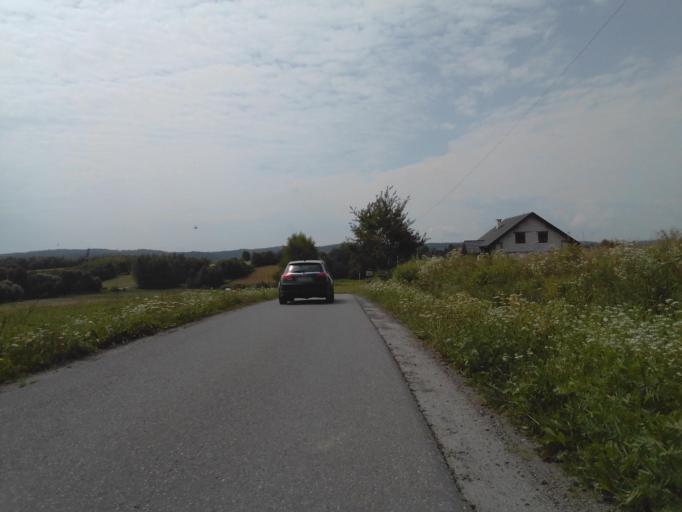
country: PL
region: Subcarpathian Voivodeship
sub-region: Powiat jasielski
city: Kolaczyce
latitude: 49.8134
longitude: 21.5065
